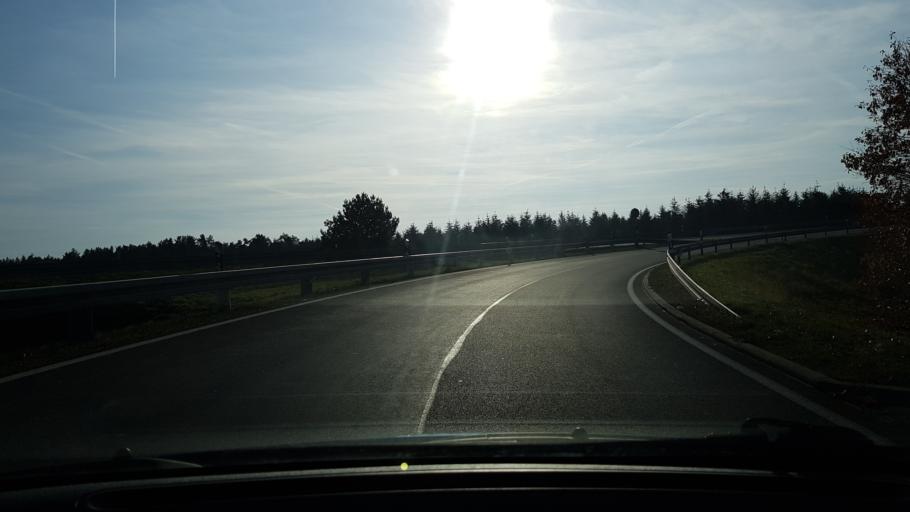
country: DE
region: Mecklenburg-Vorpommern
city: Stralendorf
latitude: 53.4848
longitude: 11.2725
